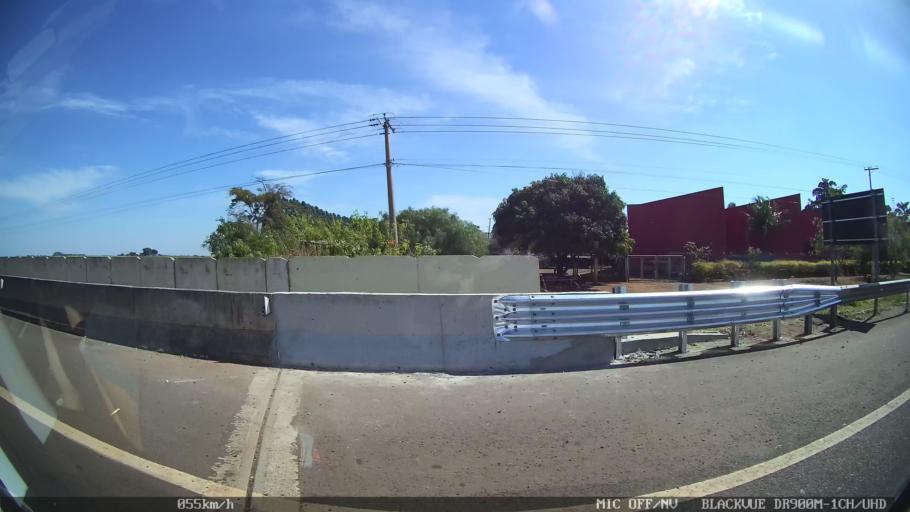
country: BR
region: Sao Paulo
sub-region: Franca
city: Franca
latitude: -20.5572
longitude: -47.4405
